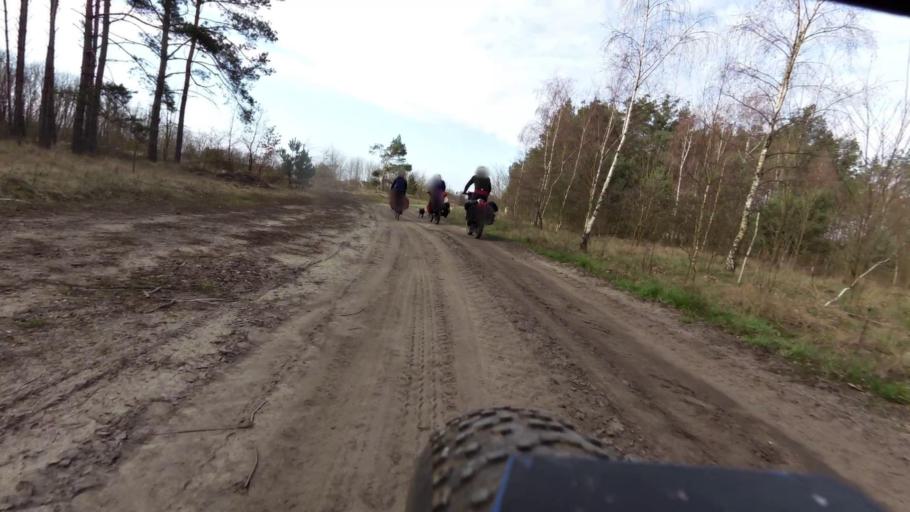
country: DE
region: Brandenburg
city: Brieskow-Finkenheerd
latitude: 52.2862
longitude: 14.6323
